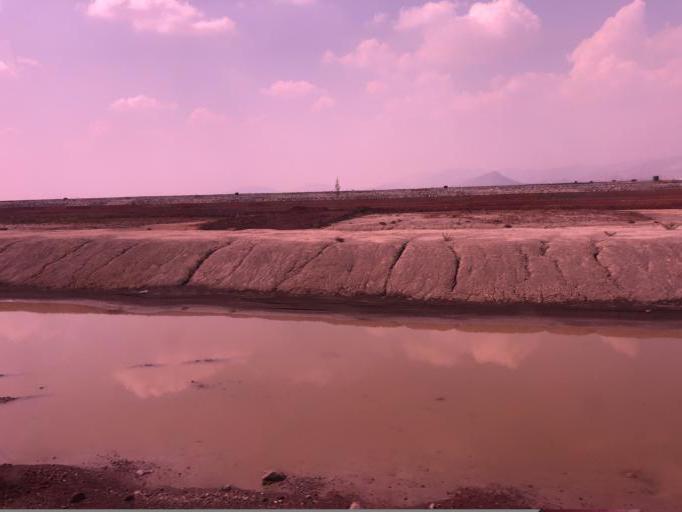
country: MX
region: Mexico
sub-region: Atenco
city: Colonia el Salado
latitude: 19.5444
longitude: -98.9850
